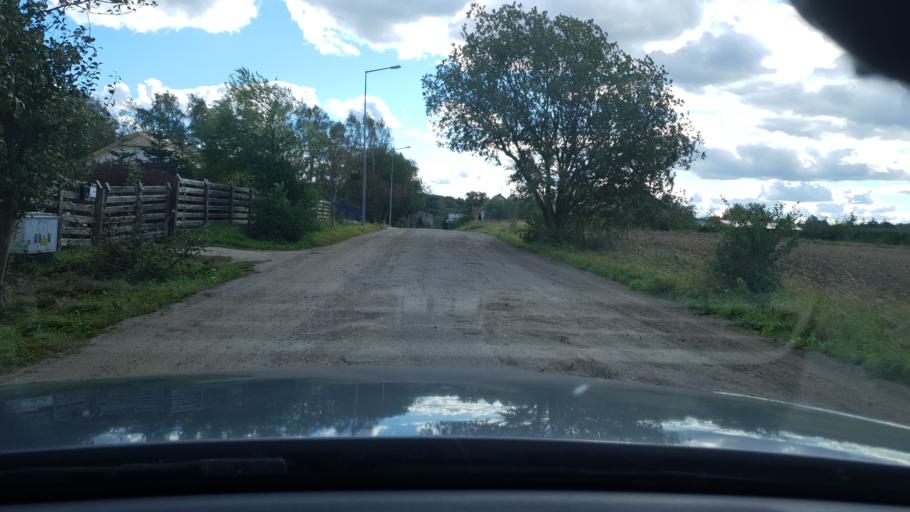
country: PL
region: Pomeranian Voivodeship
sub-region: Powiat wejherowski
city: Reda
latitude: 54.5759
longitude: 18.3095
